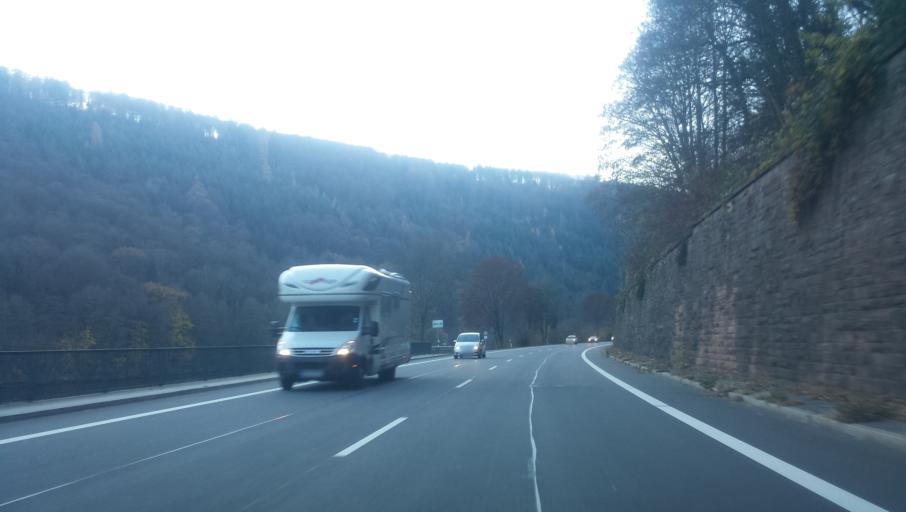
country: DE
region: Baden-Wuerttemberg
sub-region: Karlsruhe Region
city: Zwingenberg
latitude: 49.4165
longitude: 9.0170
